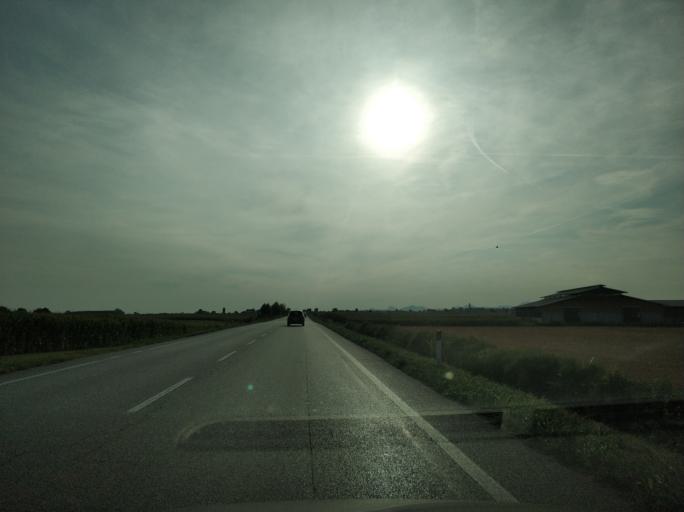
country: IT
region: Veneto
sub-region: Provincia di Venezia
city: Pegolotte
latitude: 45.2134
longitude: 12.0219
